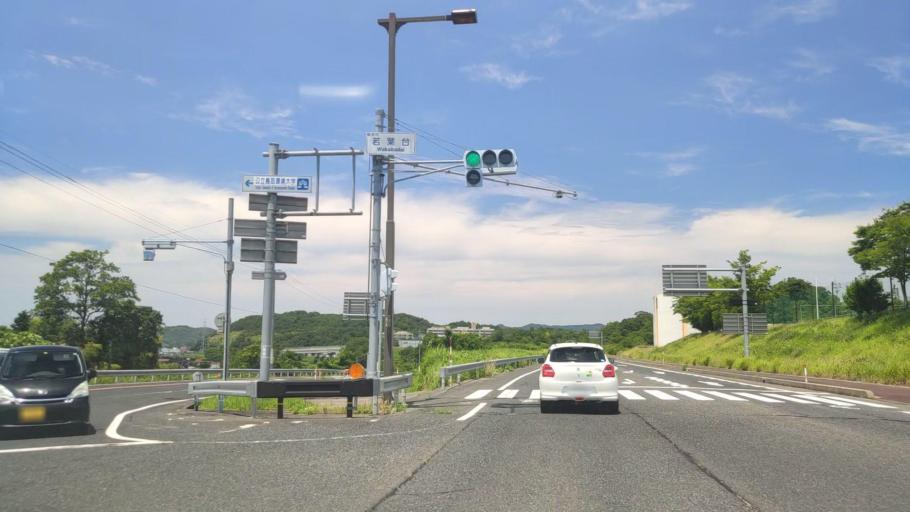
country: JP
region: Tottori
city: Tottori
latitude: 35.4426
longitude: 134.2558
